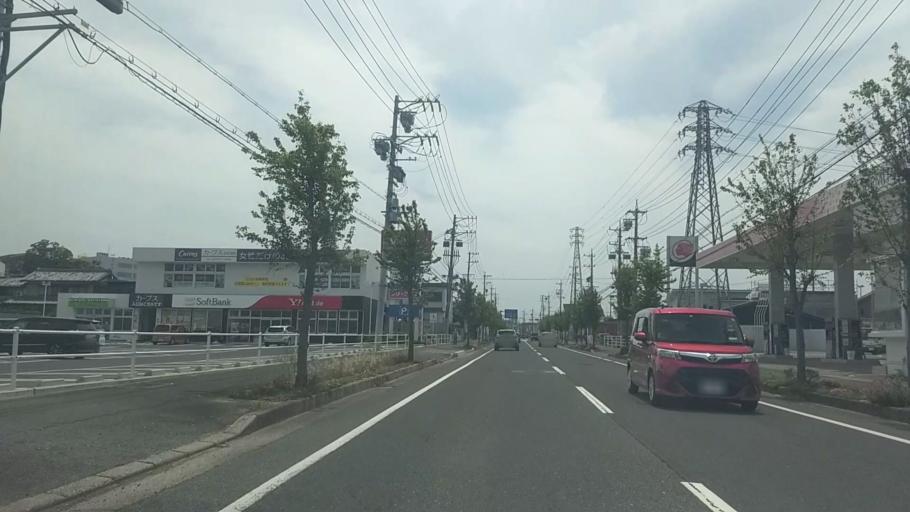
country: JP
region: Shizuoka
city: Kosai-shi
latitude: 34.7170
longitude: 137.5346
